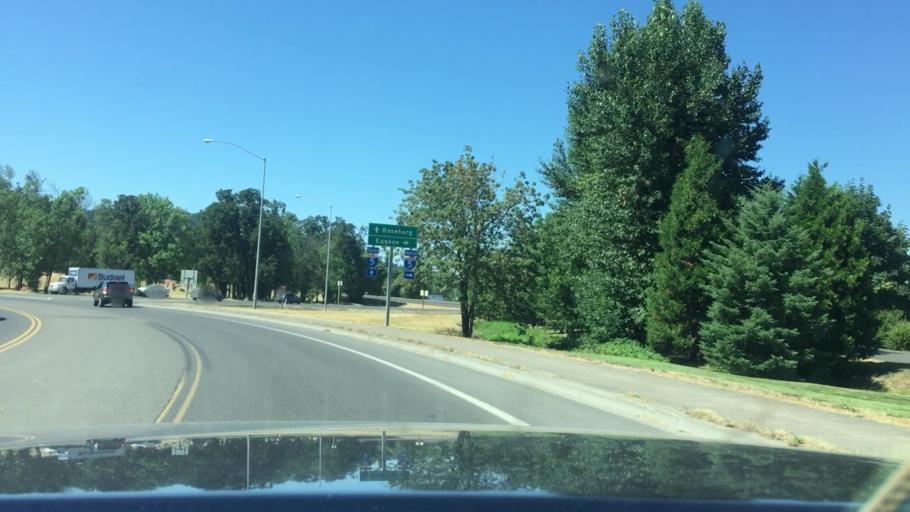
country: US
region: Oregon
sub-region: Lane County
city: Cottage Grove
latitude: 43.8040
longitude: -123.0409
